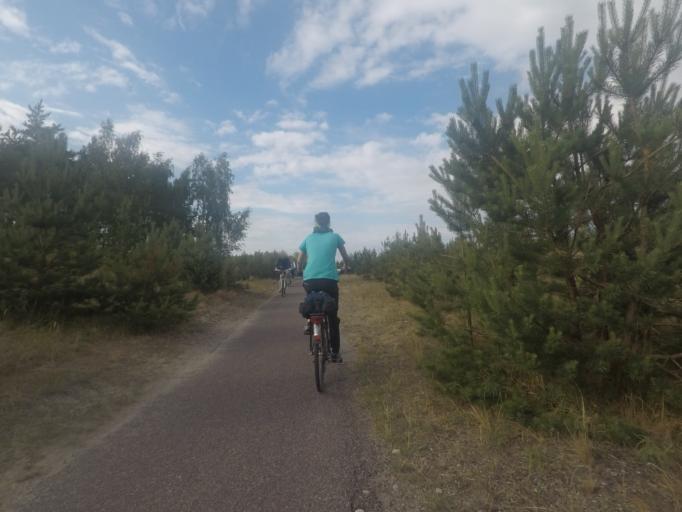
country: LT
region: Klaipedos apskritis
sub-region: Klaipeda
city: Klaipeda
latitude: 55.6344
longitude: 21.1166
